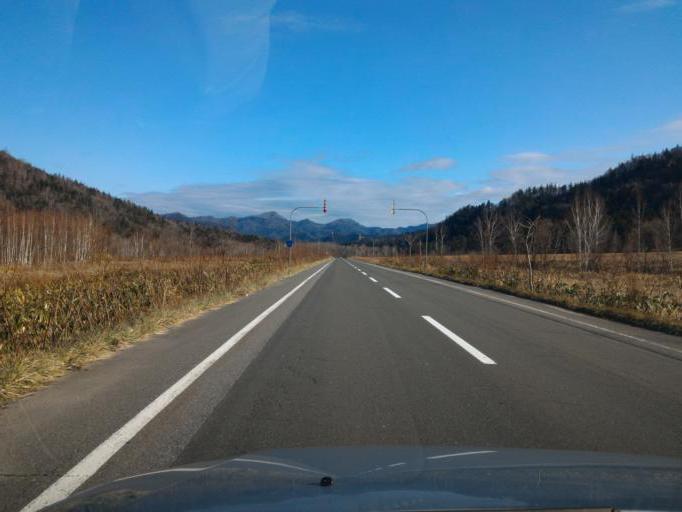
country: JP
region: Hokkaido
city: Ashibetsu
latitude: 43.3051
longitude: 142.1181
